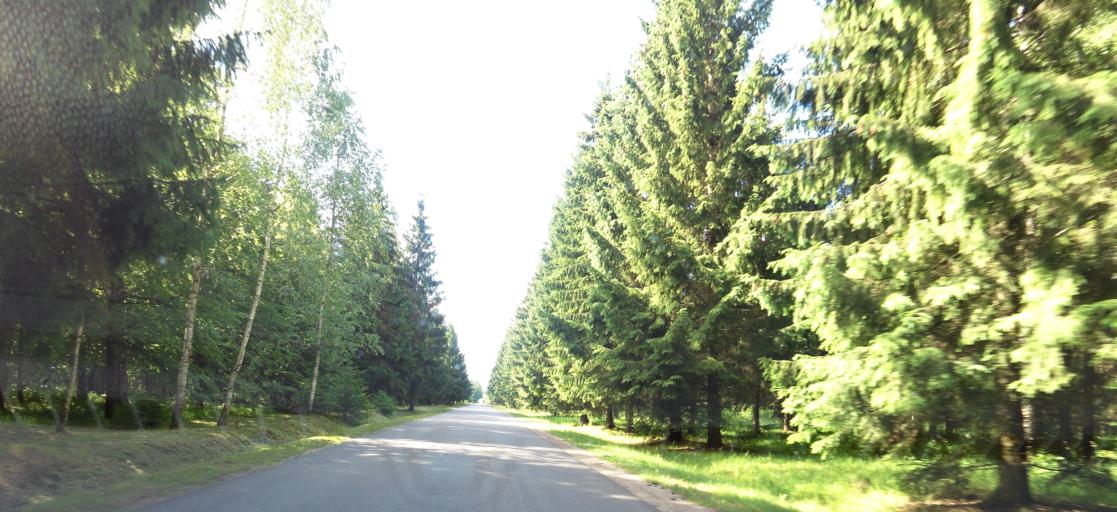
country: LT
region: Panevezys
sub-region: Birzai
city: Birzai
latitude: 56.1864
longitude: 24.7594
